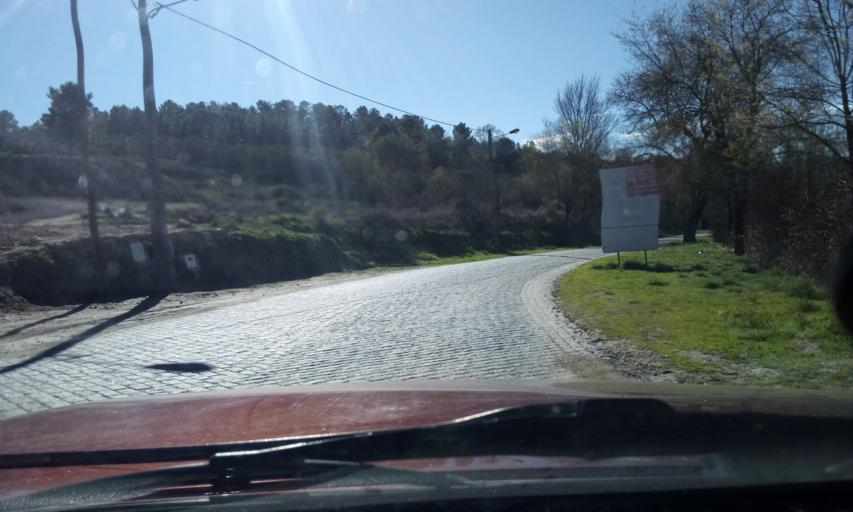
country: PT
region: Guarda
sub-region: Fornos de Algodres
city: Fornos de Algodres
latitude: 40.6245
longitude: -7.5289
